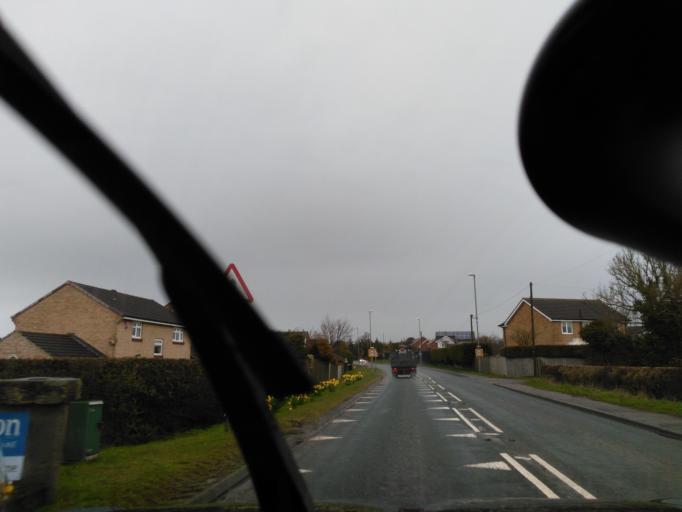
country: GB
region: England
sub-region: North Yorkshire
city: Northallerton
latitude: 54.3282
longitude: -1.4264
